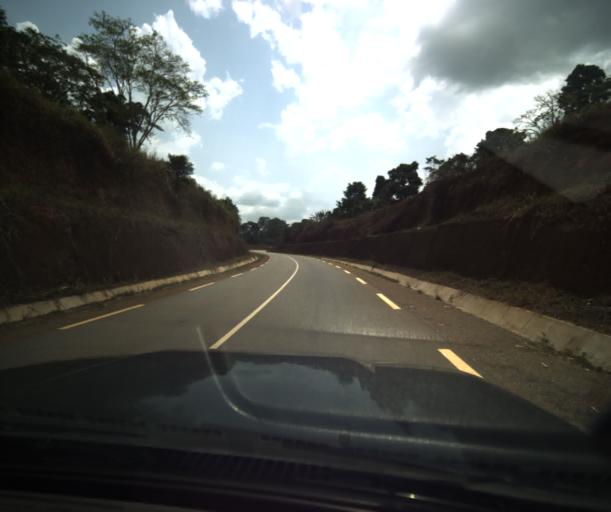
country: CM
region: Centre
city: Mbankomo
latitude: 3.6698
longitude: 11.3462
